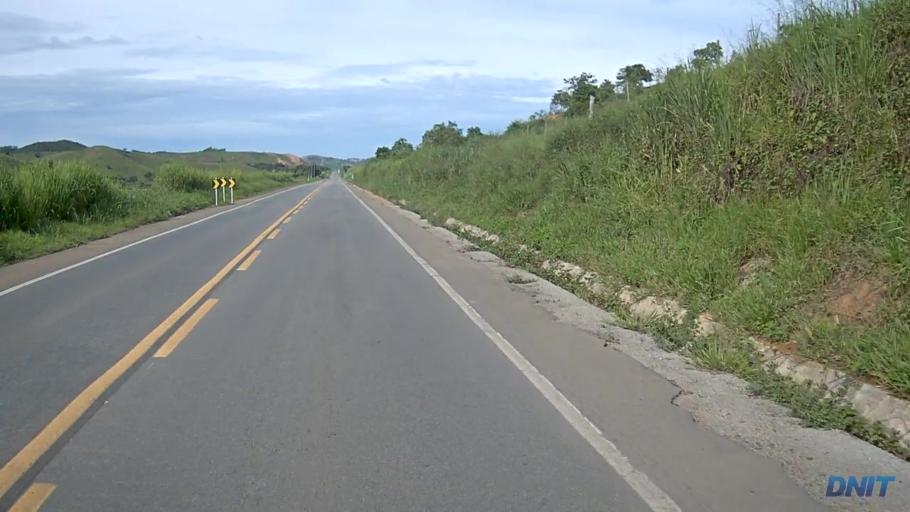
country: BR
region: Minas Gerais
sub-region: Belo Oriente
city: Belo Oriente
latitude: -19.1969
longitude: -42.2832
